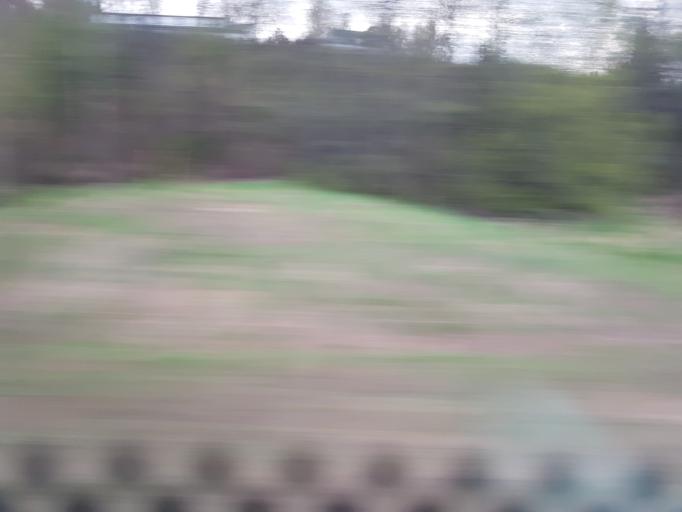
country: NO
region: Hedmark
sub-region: Ringsaker
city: Moelv
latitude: 60.9123
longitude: 10.7364
